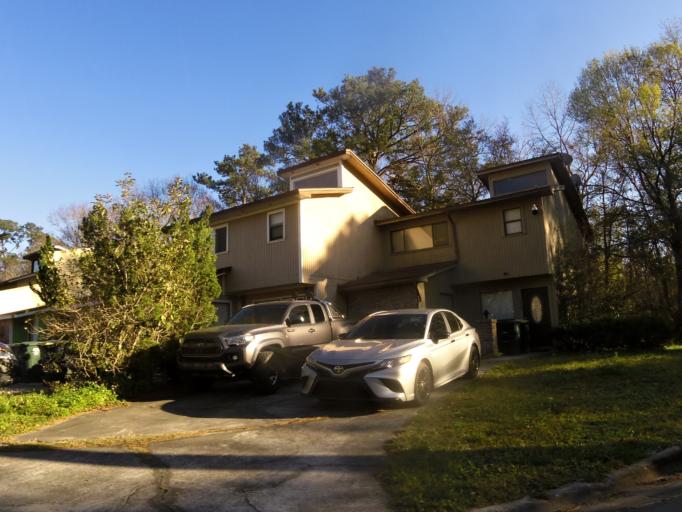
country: US
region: Florida
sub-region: Duval County
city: Jacksonville
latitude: 30.2290
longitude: -81.5996
